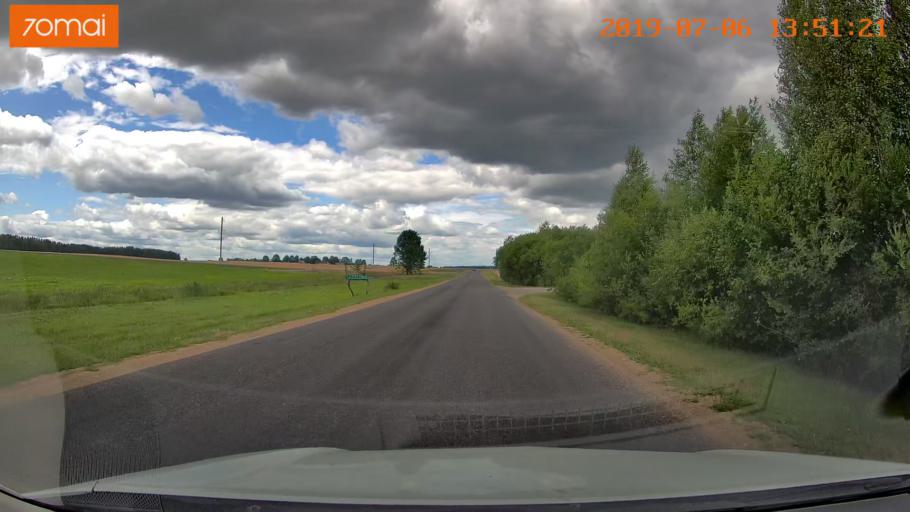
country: BY
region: Minsk
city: Ivyanyets
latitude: 53.7073
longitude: 26.8330
